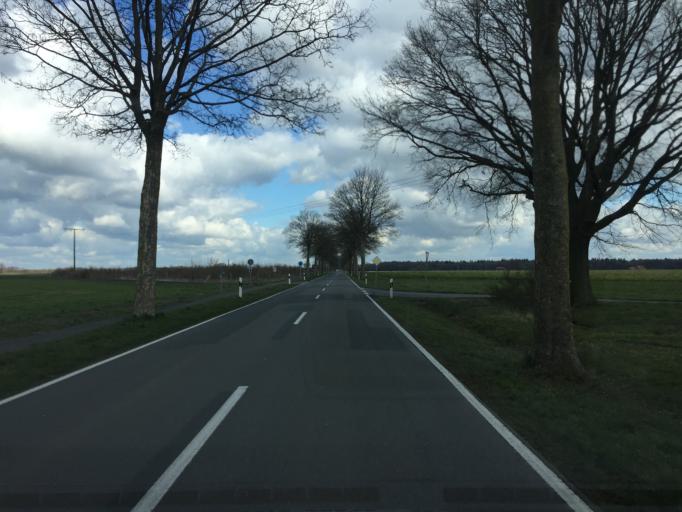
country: DE
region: Lower Saxony
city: Schwaforden
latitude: 52.7555
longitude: 8.8384
